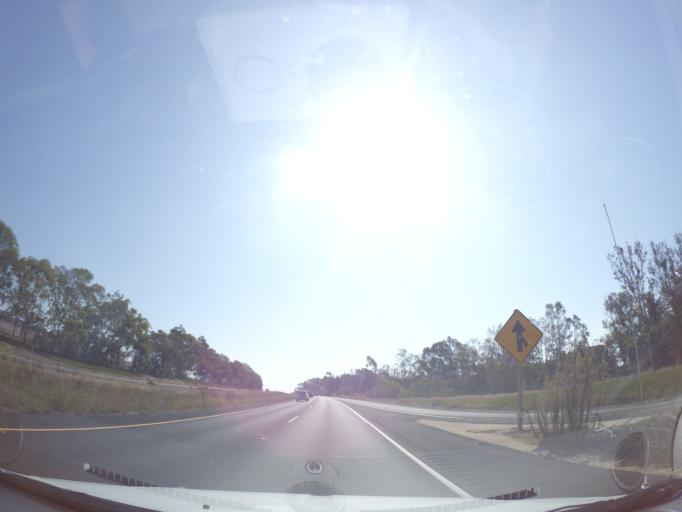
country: US
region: California
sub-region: Santa Barbara County
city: Isla Vista
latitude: 34.4439
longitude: -119.9544
